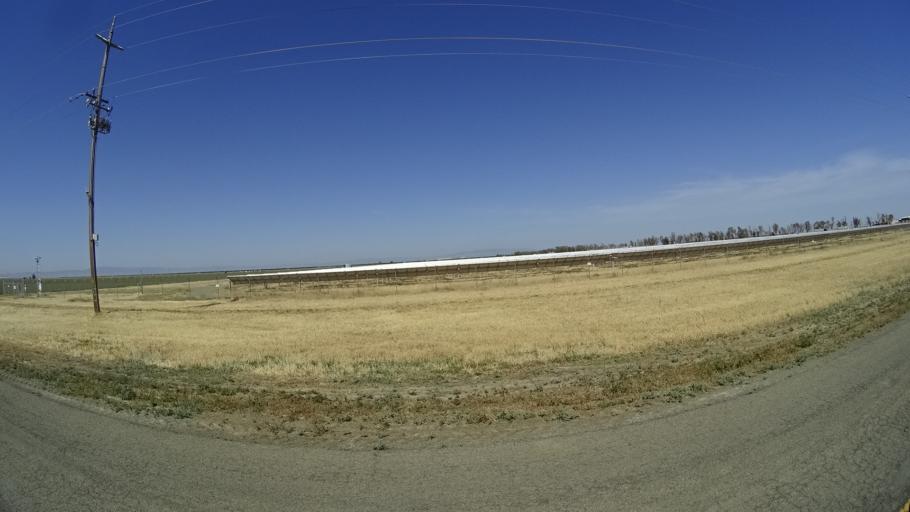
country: US
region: California
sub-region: Kings County
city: Lemoore Station
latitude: 36.2511
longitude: -119.9051
